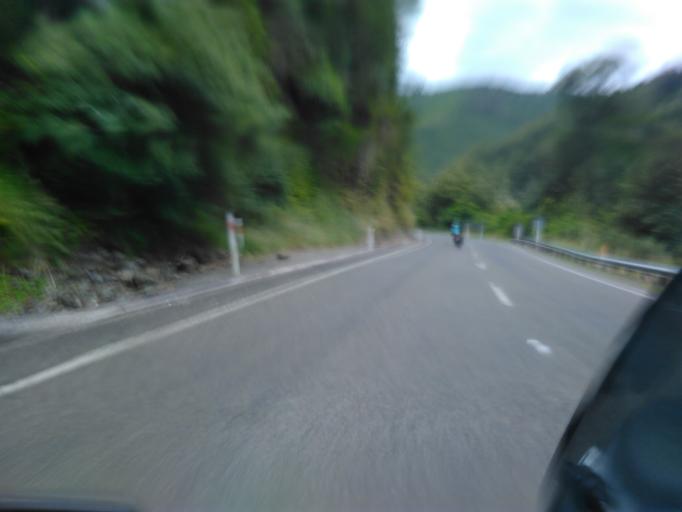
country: NZ
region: Bay of Plenty
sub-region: Opotiki District
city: Opotiki
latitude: -38.2710
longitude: 177.3216
